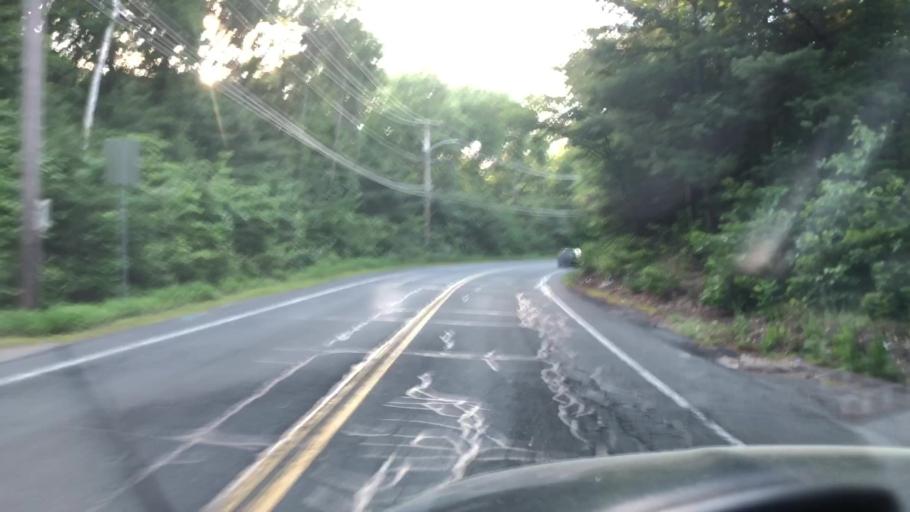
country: US
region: Massachusetts
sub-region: Hampden County
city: Holyoke
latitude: 42.2248
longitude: -72.6456
